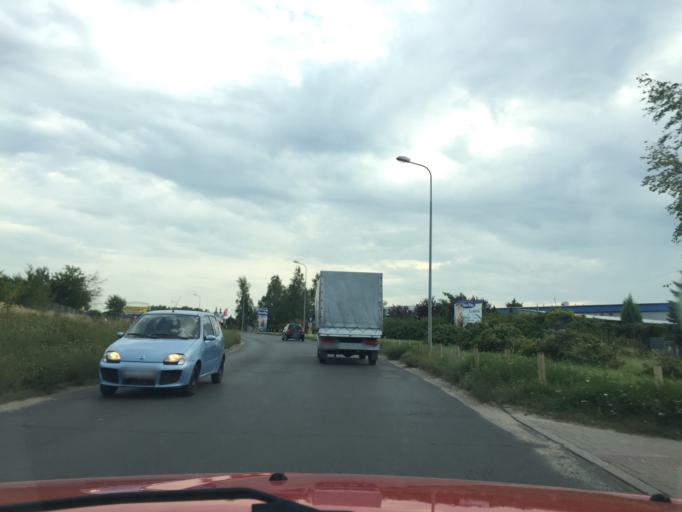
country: PL
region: Greater Poland Voivodeship
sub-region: Powiat poznanski
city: Baranowo
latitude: 52.4271
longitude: 16.7980
